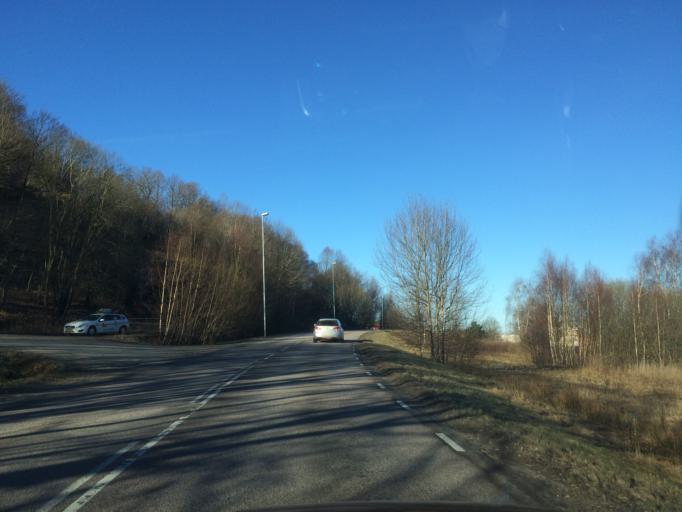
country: SE
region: Vaestra Goetaland
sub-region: Molndal
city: Moelndal
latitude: 57.6404
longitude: 12.0056
